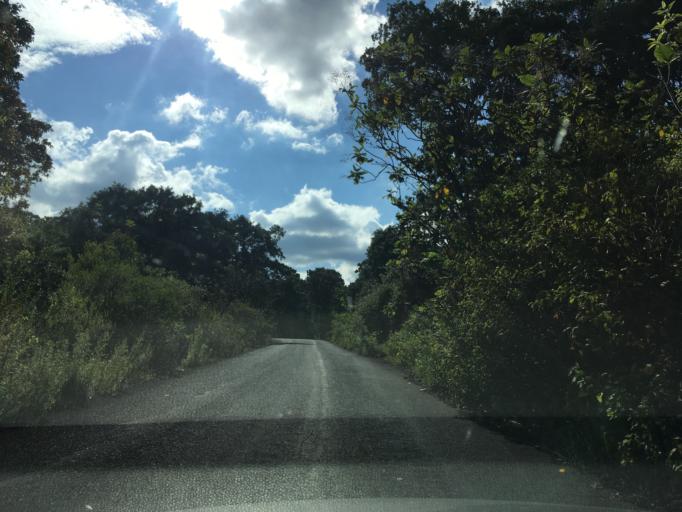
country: MX
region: Michoacan
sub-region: Zacapu
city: Naranja de Tapia
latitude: 19.7506
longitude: -101.7931
